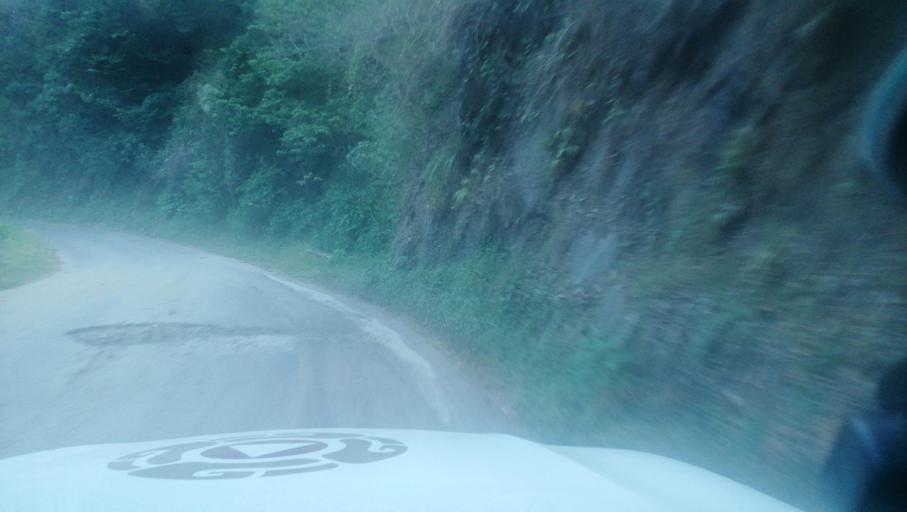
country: MX
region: Chiapas
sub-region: Cacahoatan
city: Benito Juarez
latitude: 15.1412
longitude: -92.1956
